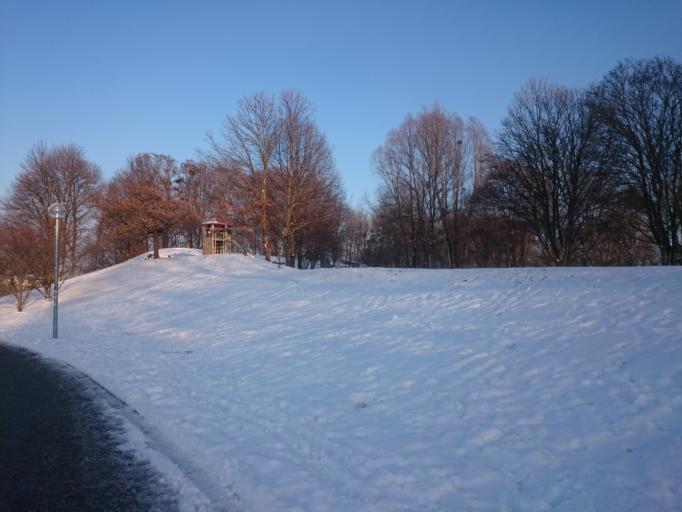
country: DE
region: Bavaria
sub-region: Upper Bavaria
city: Munich
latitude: 48.1724
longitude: 11.5579
